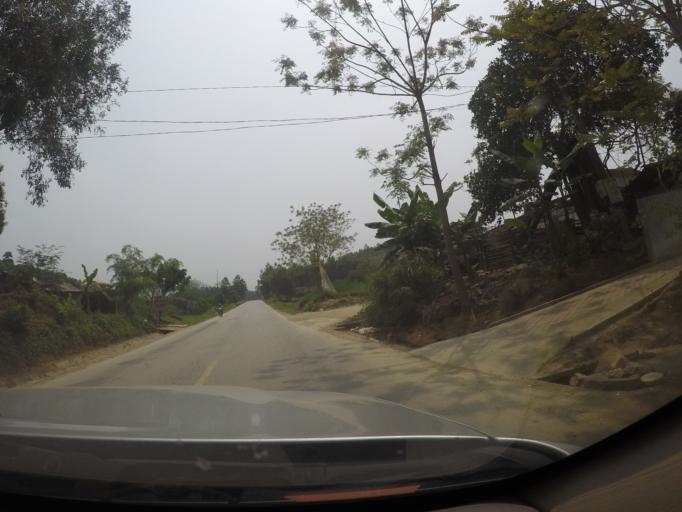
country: VN
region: Thanh Hoa
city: Thi Tran Thuong Xuan
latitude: 19.8219
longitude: 105.3909
